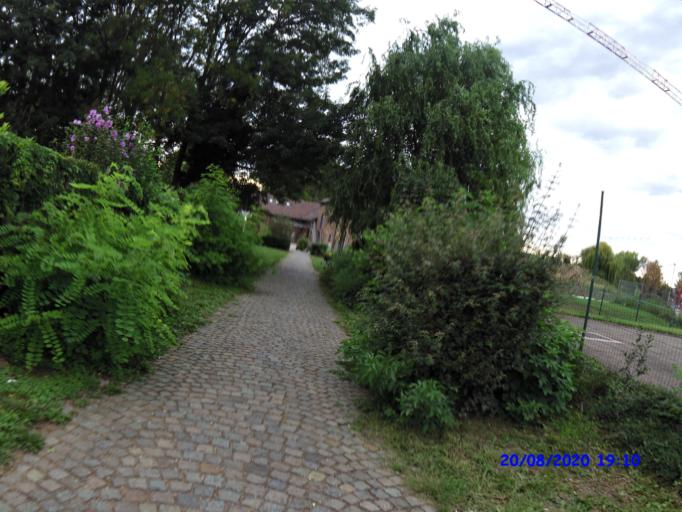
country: BE
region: Flanders
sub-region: Provincie Limburg
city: Sint-Truiden
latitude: 50.8093
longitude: 5.1811
